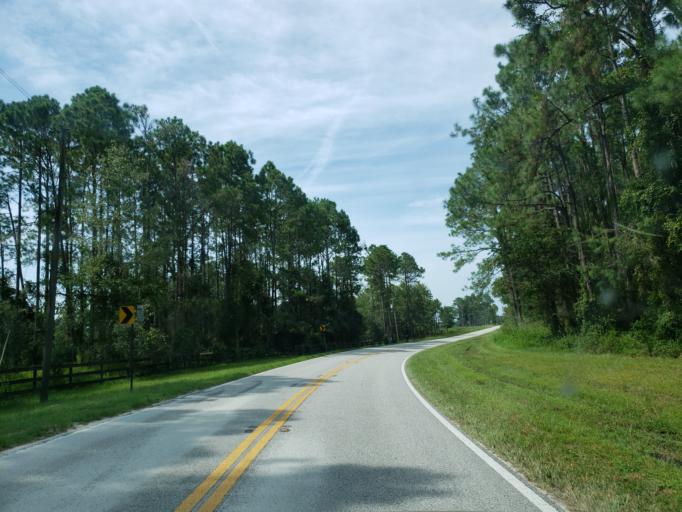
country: US
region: Florida
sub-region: Pasco County
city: San Antonio
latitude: 28.3922
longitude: -82.3117
